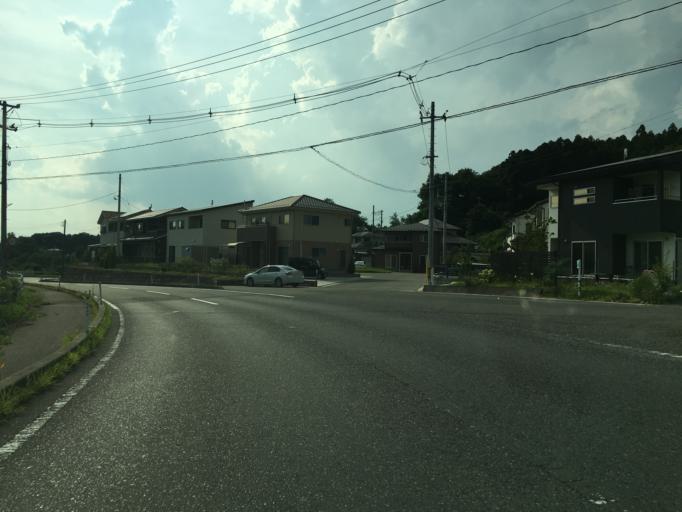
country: JP
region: Fukushima
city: Miharu
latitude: 37.4464
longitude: 140.4351
